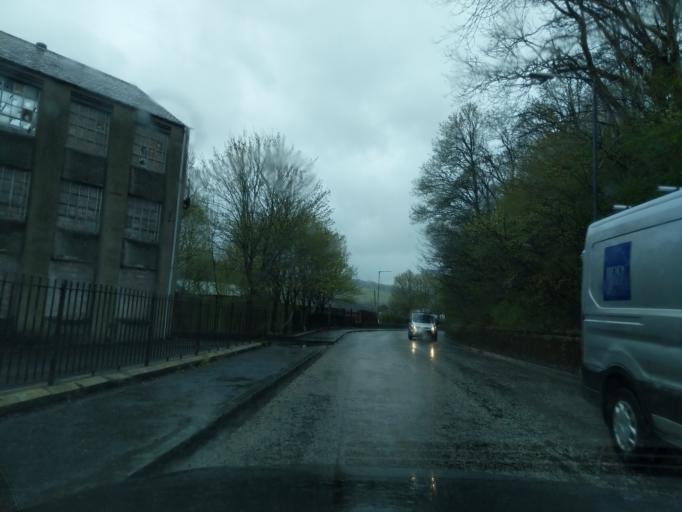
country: GB
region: Scotland
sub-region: The Scottish Borders
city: Selkirk
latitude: 55.5501
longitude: -2.8452
